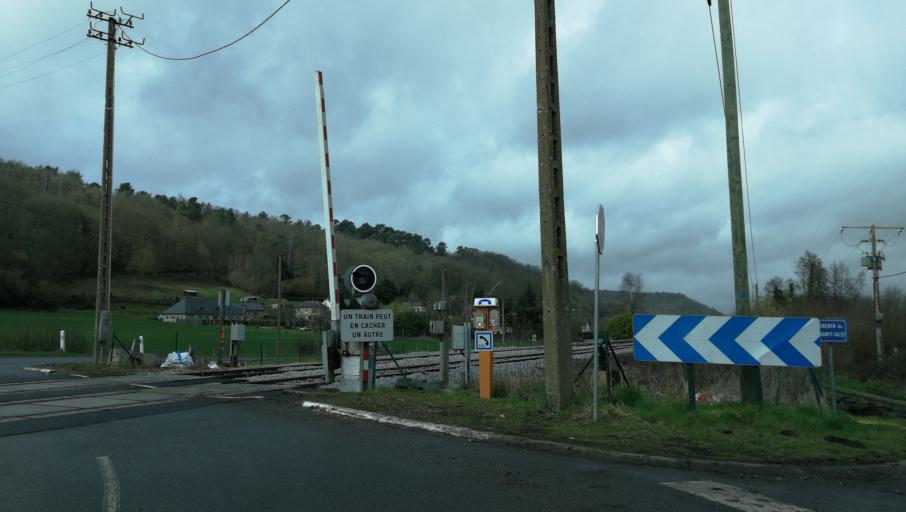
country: FR
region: Haute-Normandie
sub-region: Departement de l'Eure
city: Brionne
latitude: 49.2217
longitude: 0.6978
